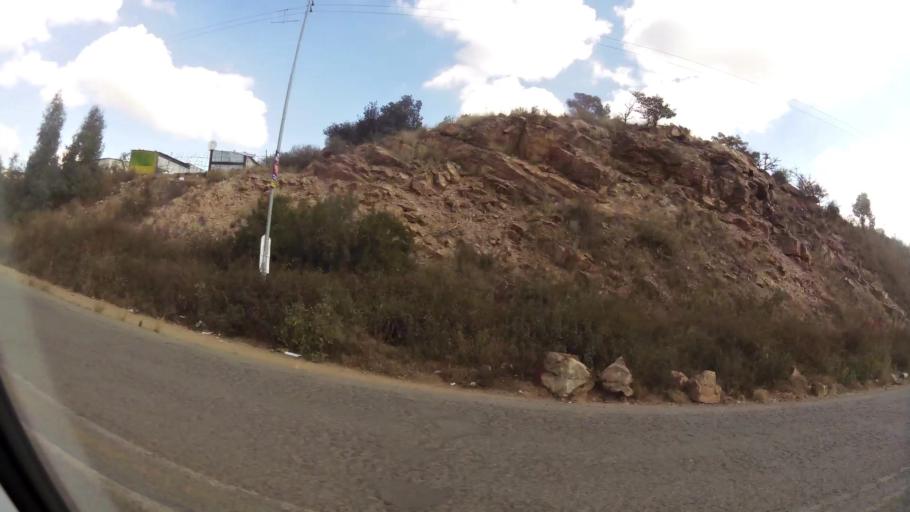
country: ZA
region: Gauteng
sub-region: City of Tshwane Metropolitan Municipality
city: Cullinan
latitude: -25.6957
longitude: 28.4200
